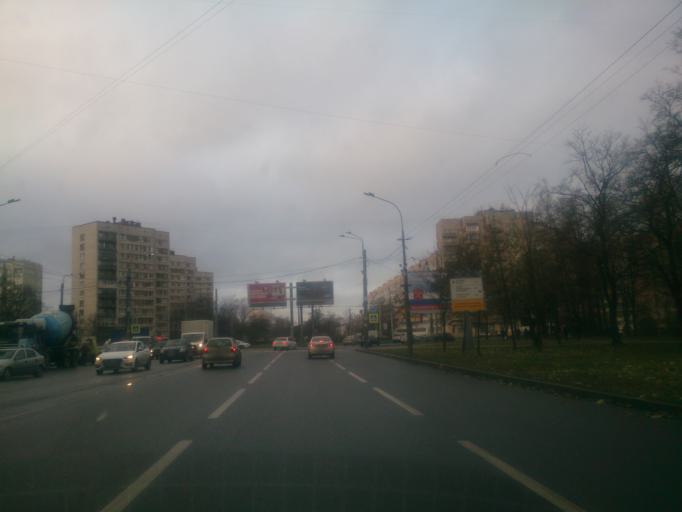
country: RU
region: St.-Petersburg
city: Dachnoye
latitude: 59.8437
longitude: 30.2515
